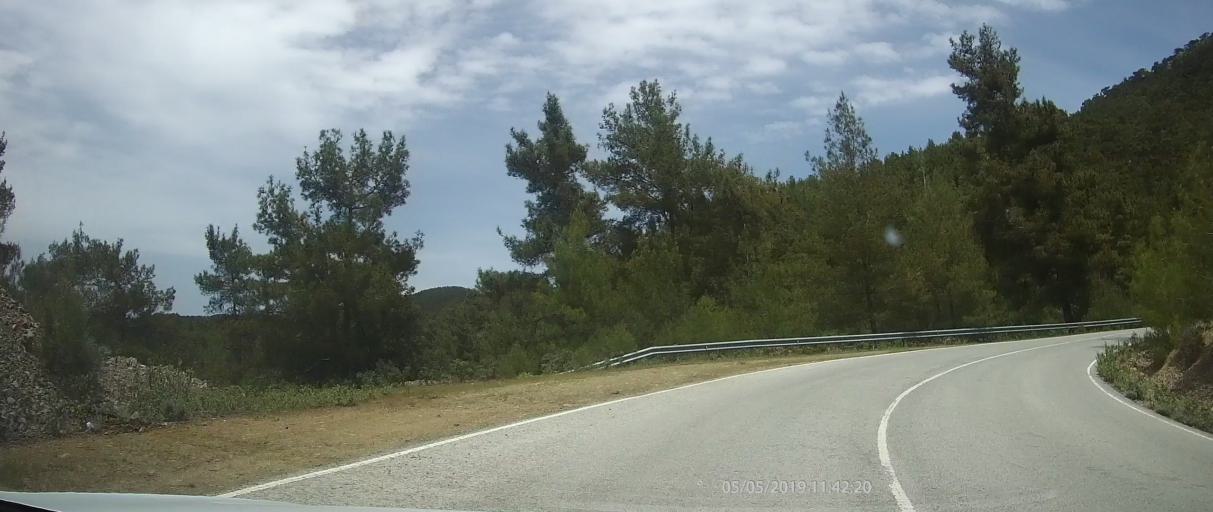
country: CY
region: Lefkosia
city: Kato Pyrgos
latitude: 35.0013
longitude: 32.6709
